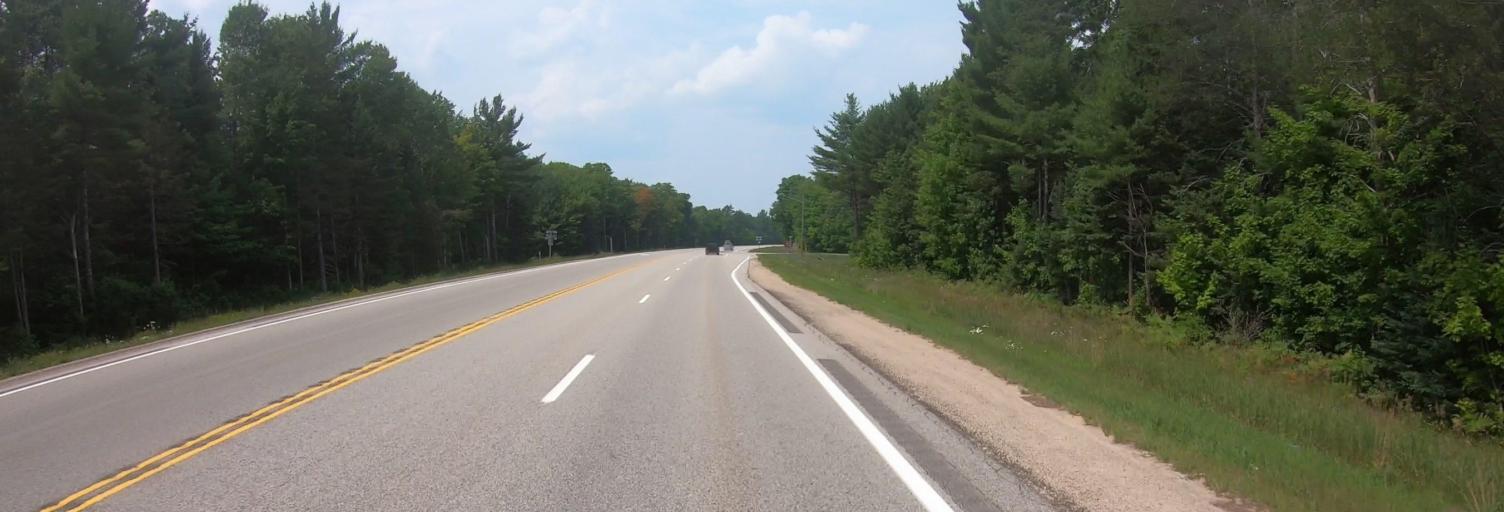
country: US
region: Michigan
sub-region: Alger County
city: Munising
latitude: 46.3482
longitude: -86.4883
